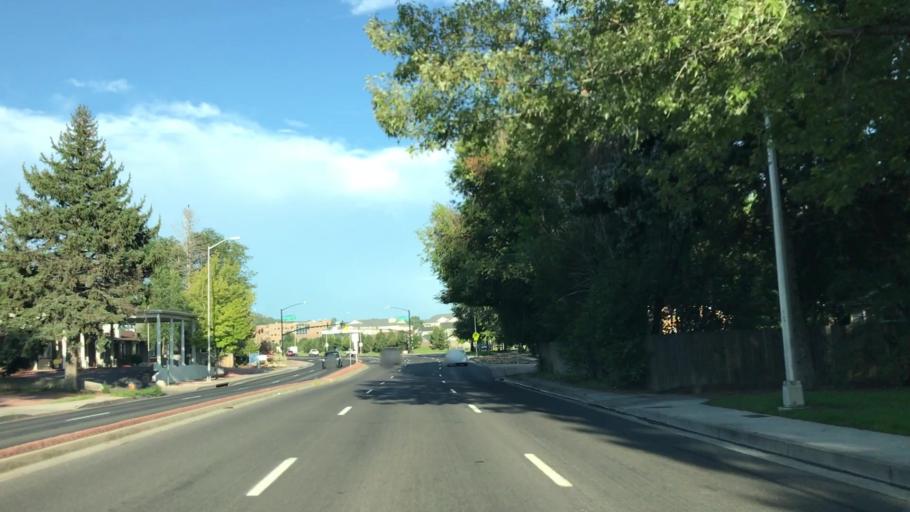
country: US
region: Colorado
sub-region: El Paso County
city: Colorado Springs
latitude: 38.8738
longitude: -104.8016
